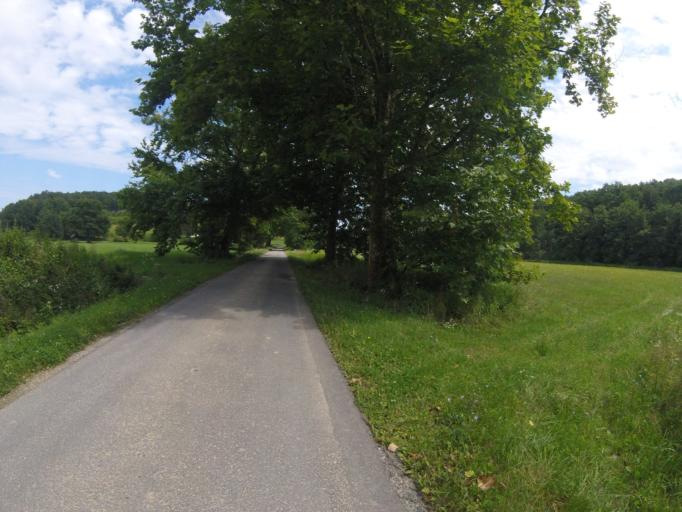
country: HU
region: Zala
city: Lenti
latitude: 46.5640
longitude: 16.6311
